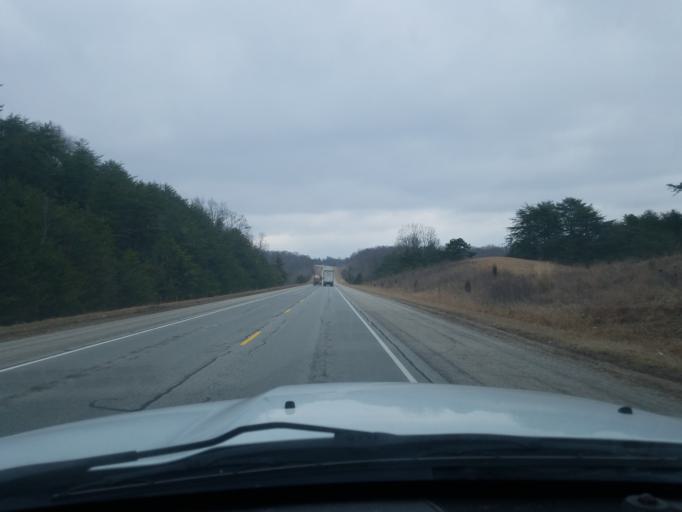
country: US
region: Indiana
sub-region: Perry County
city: Tell City
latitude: 38.0533
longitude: -86.6326
